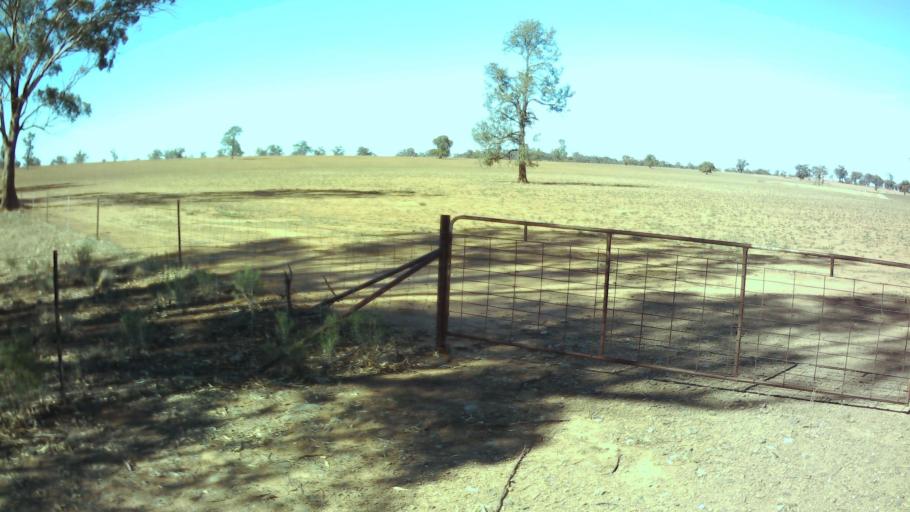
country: AU
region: New South Wales
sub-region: Weddin
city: Grenfell
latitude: -33.7405
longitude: 147.8321
